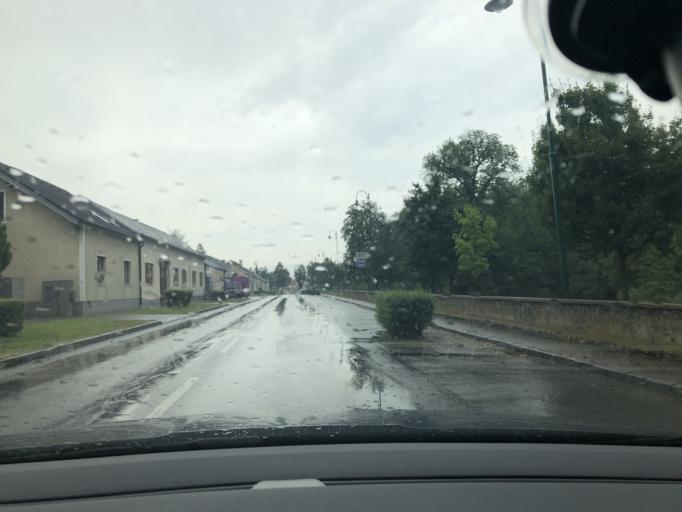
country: AT
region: Lower Austria
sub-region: Politischer Bezirk Ganserndorf
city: Ganserndorf
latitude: 48.3678
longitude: 16.6929
